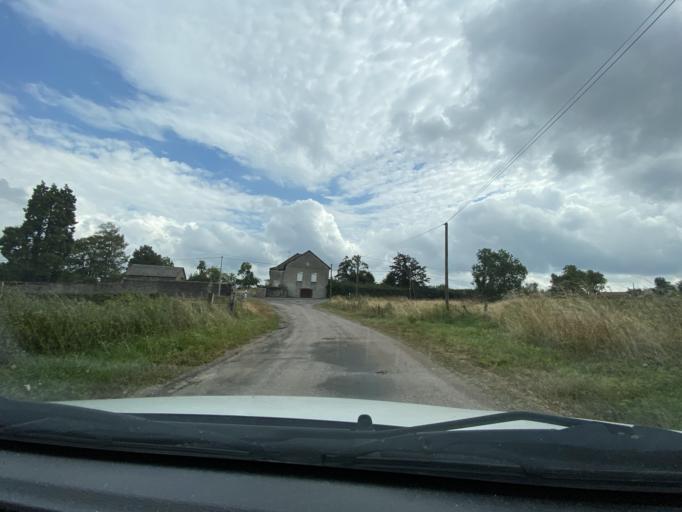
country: FR
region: Bourgogne
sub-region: Departement de la Cote-d'Or
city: Saulieu
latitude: 47.2849
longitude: 4.2381
